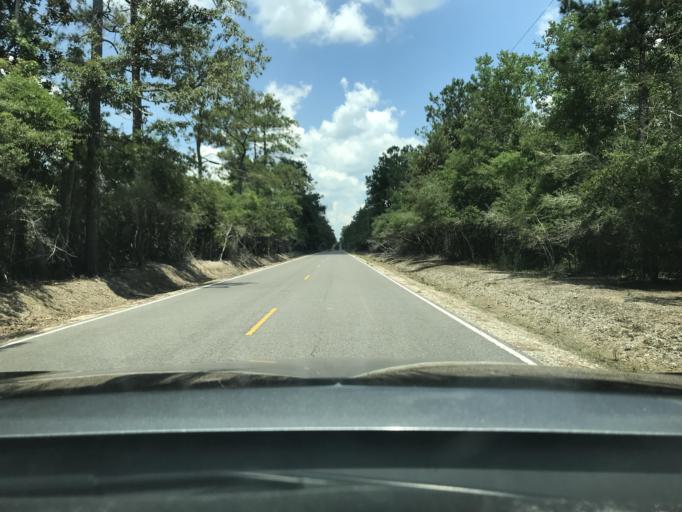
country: US
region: Louisiana
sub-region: Calcasieu Parish
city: Moss Bluff
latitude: 30.3299
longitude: -93.1456
